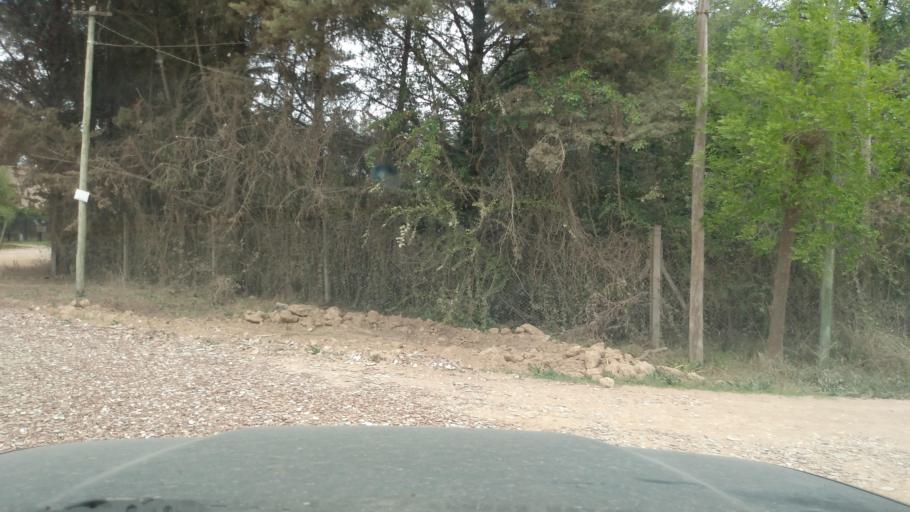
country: AR
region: Buenos Aires
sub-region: Partido de Lujan
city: Lujan
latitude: -34.5920
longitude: -59.1338
